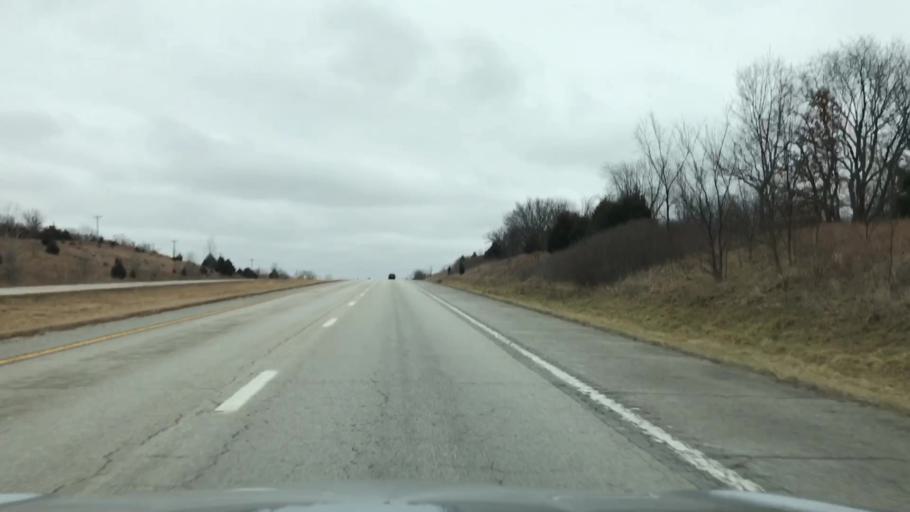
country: US
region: Missouri
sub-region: Clinton County
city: Cameron
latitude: 39.7512
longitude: -94.1536
